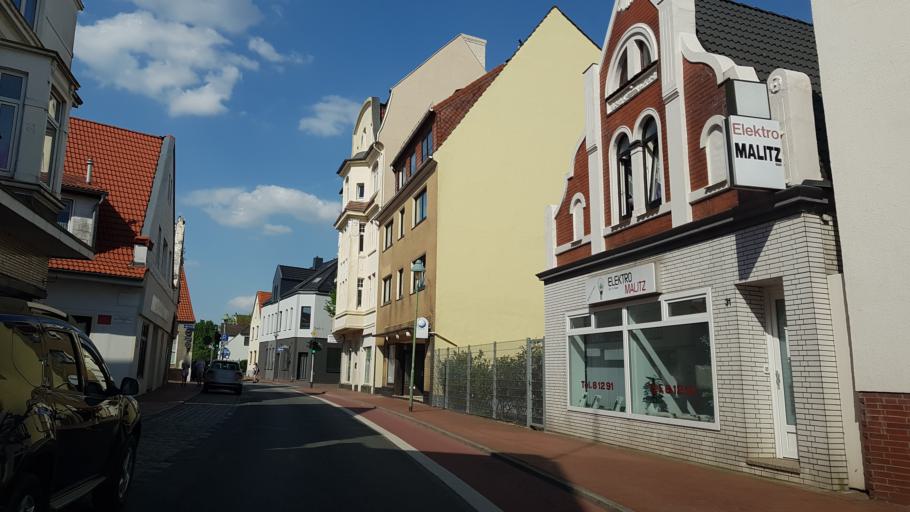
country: DE
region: Bremen
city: Bremerhaven
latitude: 53.5696
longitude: 8.5945
